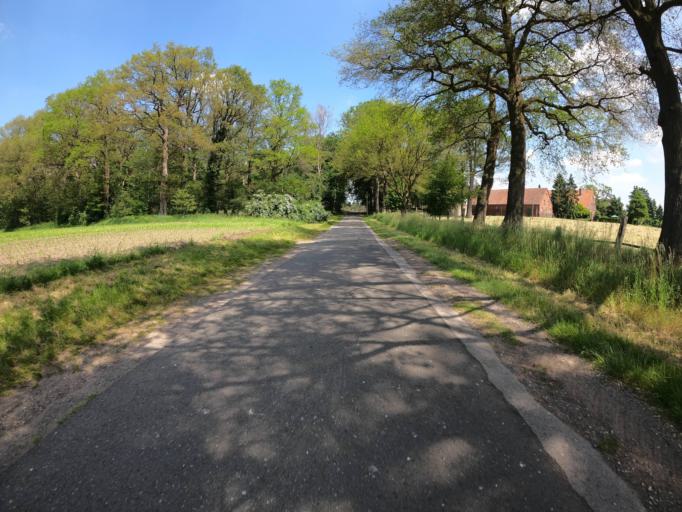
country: DE
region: North Rhine-Westphalia
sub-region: Regierungsbezirk Dusseldorf
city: Hunxe
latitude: 51.7099
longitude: 6.7129
